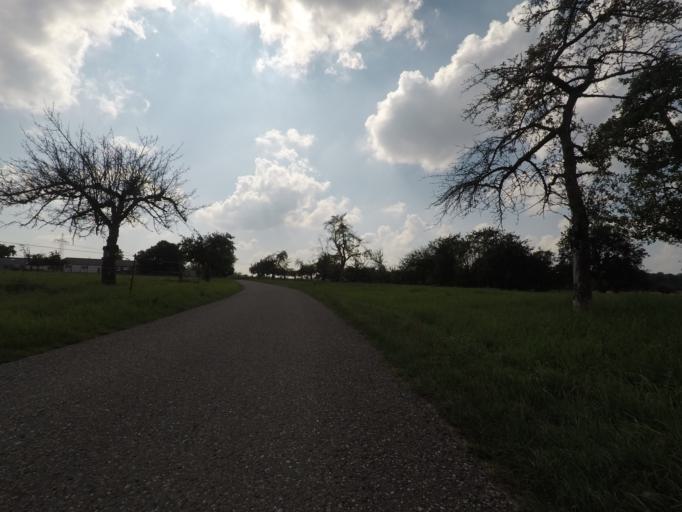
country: DE
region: Baden-Wuerttemberg
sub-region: Regierungsbezirk Stuttgart
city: Altbach
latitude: 48.7530
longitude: 9.3824
